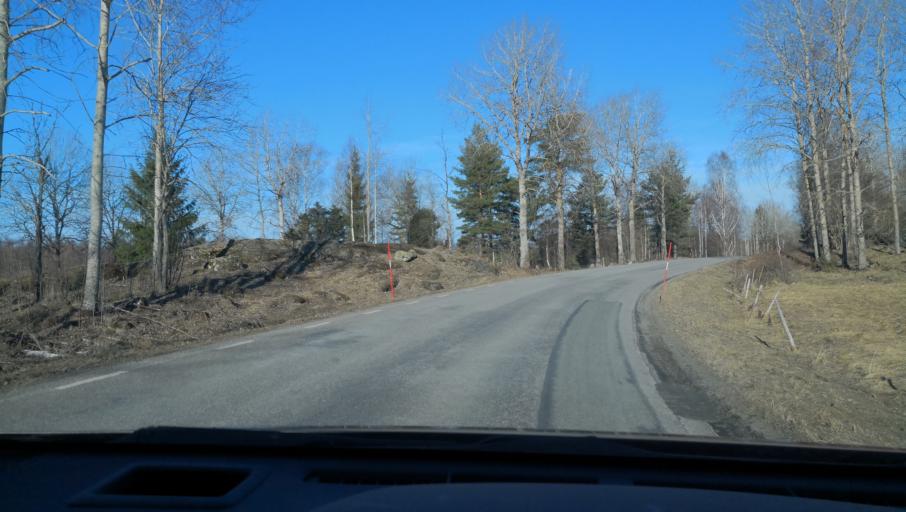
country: SE
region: Uppsala
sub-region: Osthammars Kommun
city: Osterbybruk
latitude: 60.2388
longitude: 17.9238
